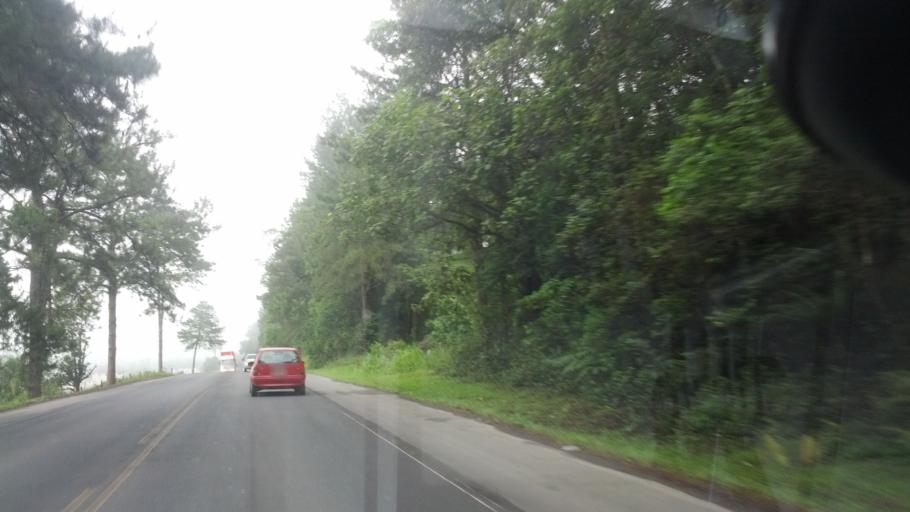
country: BR
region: Santa Catarina
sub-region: Rio Do Sul
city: Rio do Sul
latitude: -27.2661
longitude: -49.7273
